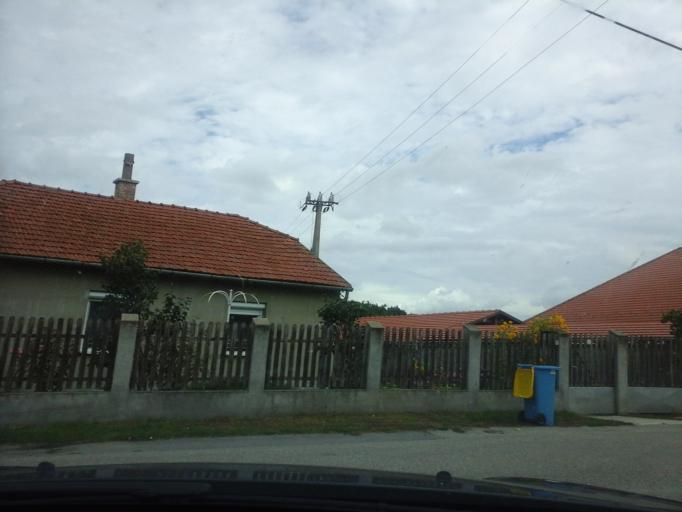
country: HU
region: Borsod-Abauj-Zemplen
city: Sajokaza
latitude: 48.3323
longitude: 20.5965
